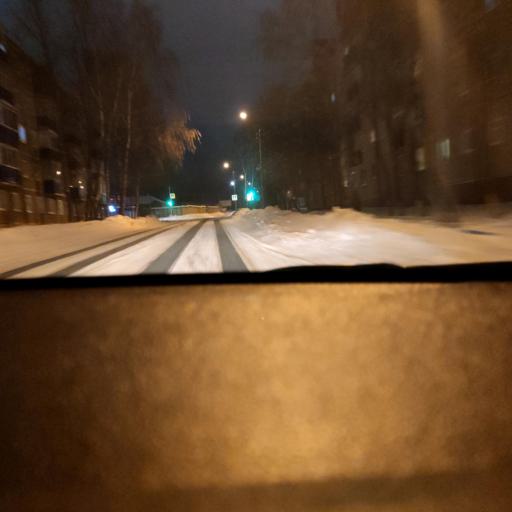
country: RU
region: Tatarstan
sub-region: Chistopol'skiy Rayon
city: Chistopol'
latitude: 55.3620
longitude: 50.6099
